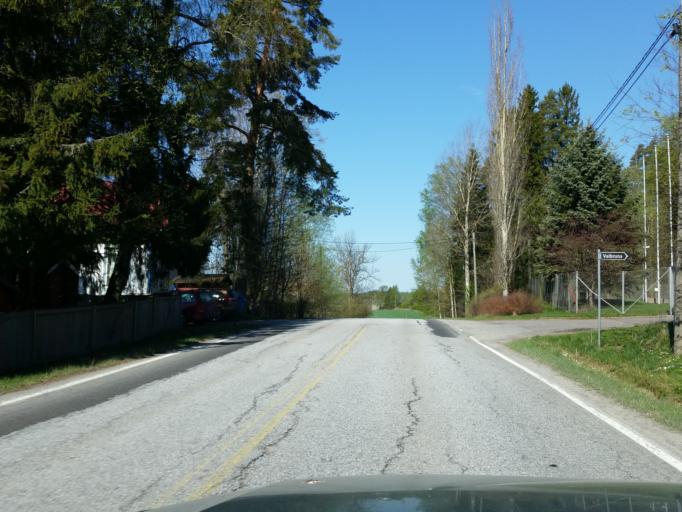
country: FI
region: Uusimaa
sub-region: Helsinki
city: Lohja
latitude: 60.1761
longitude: 24.0906
